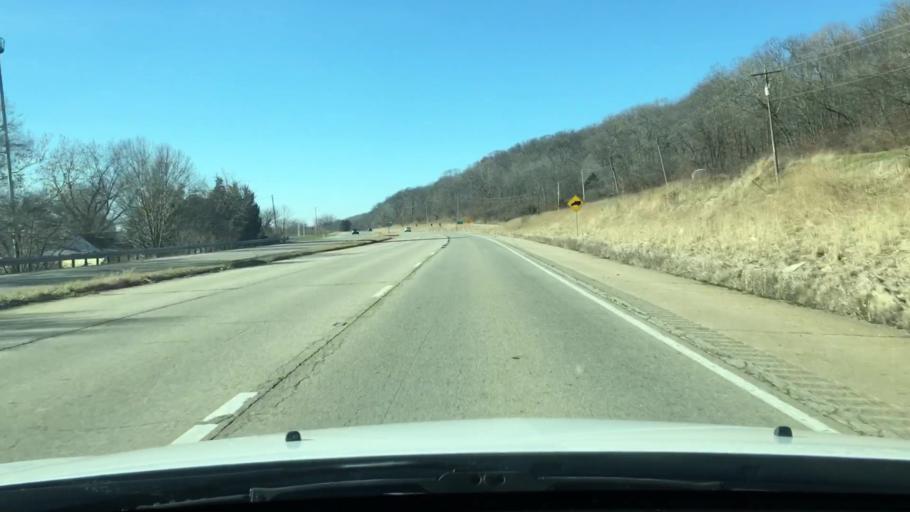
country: US
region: Illinois
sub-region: Peoria County
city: Glasford
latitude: 40.5589
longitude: -89.7734
